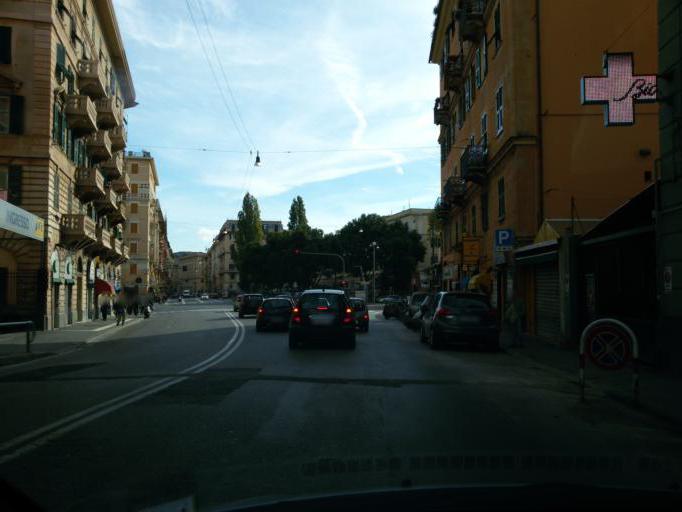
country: IT
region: Liguria
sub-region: Provincia di Genova
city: Genoa
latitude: 44.4077
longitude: 8.9521
